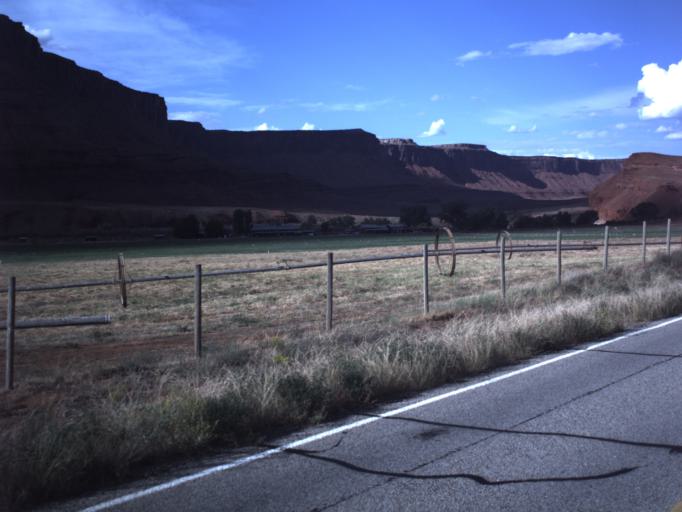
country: US
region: Utah
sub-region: Grand County
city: Moab
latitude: 38.6961
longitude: -109.4009
